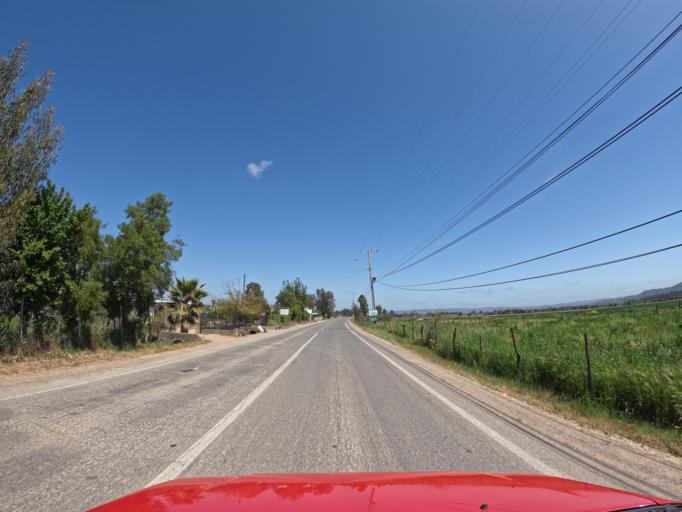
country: CL
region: O'Higgins
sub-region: Provincia de Colchagua
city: Santa Cruz
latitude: -34.7295
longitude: -71.6696
